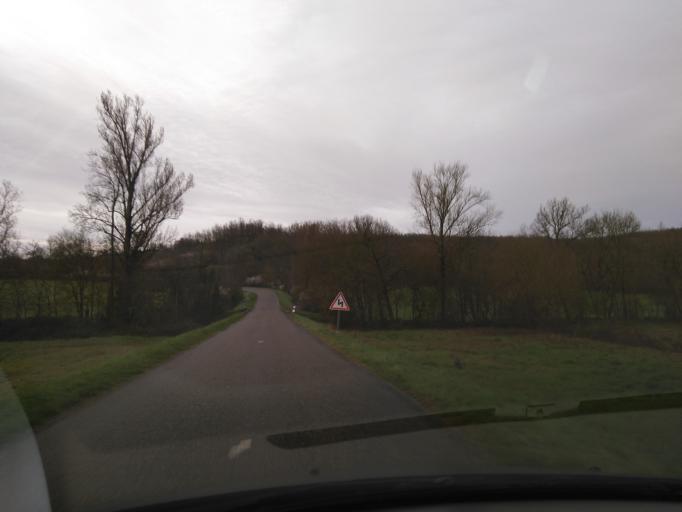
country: FR
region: Midi-Pyrenees
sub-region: Departement du Tarn-et-Garonne
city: Finhan
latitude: 43.8799
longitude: 1.1456
